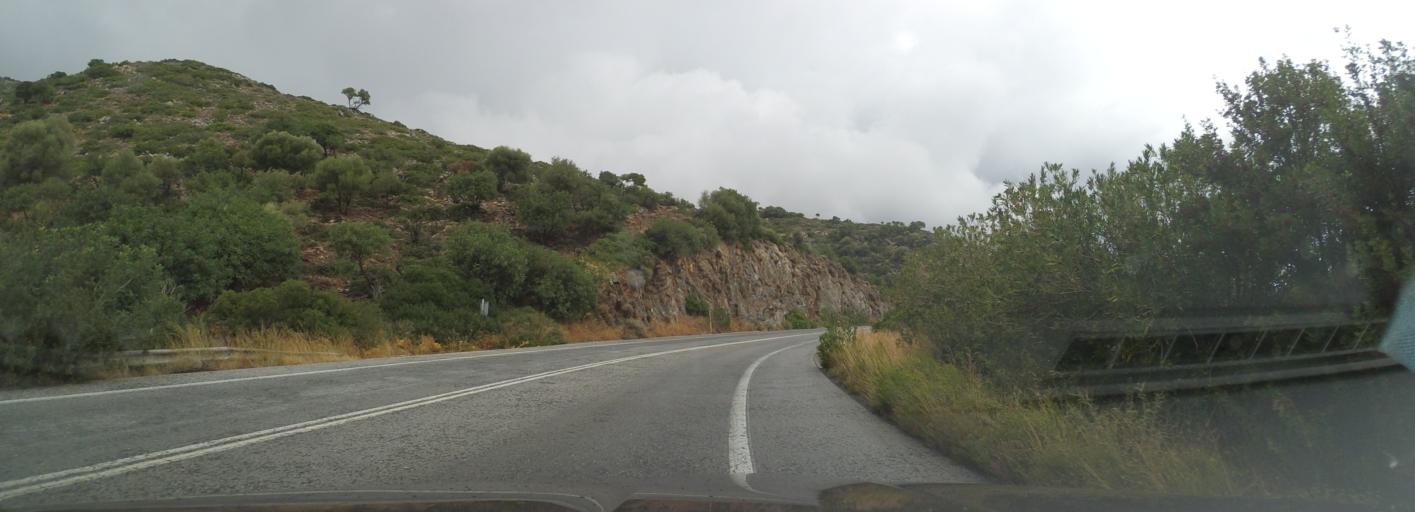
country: GR
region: Crete
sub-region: Nomos Rethymnis
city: Anogeia
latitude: 35.3829
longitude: 24.9159
